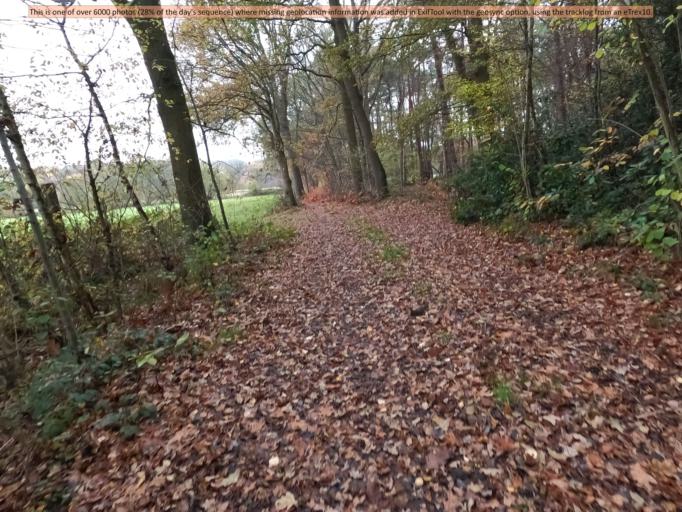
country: BE
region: Flanders
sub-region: Provincie Antwerpen
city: Nijlen
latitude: 51.1364
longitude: 4.7030
